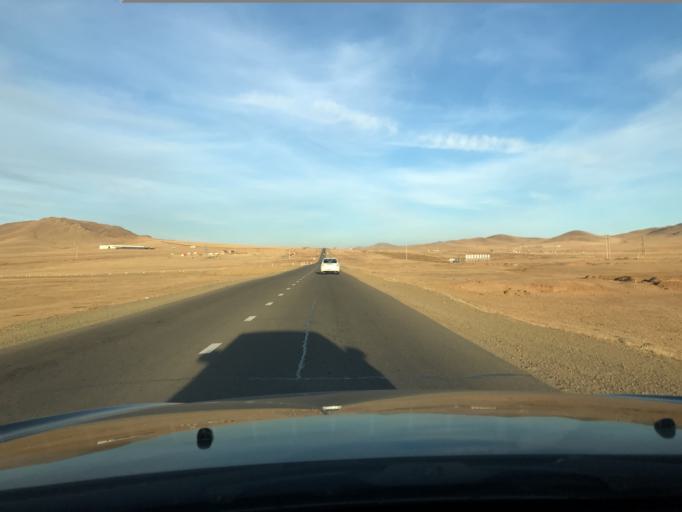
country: MN
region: Central Aimak
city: Arhust
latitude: 47.7919
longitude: 107.4842
